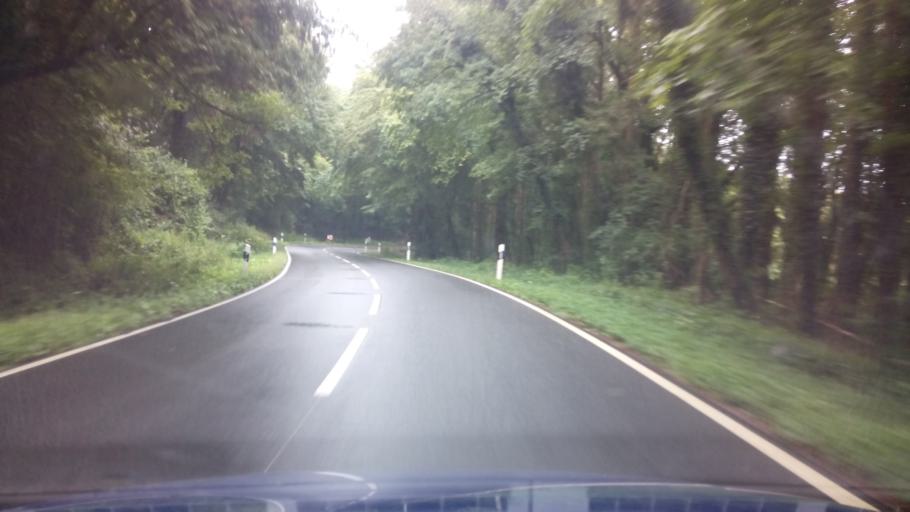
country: DE
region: Lower Saxony
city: Melle
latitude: 52.2430
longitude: 8.3097
